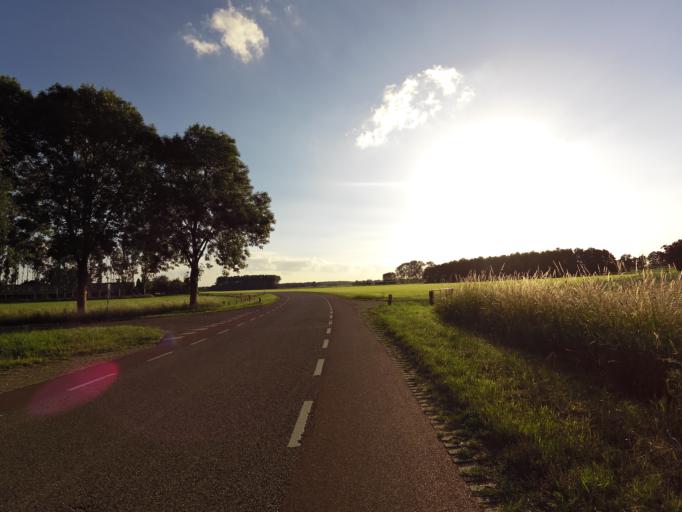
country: NL
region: Gelderland
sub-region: Oude IJsselstreek
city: Wisch
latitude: 51.8837
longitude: 6.4255
